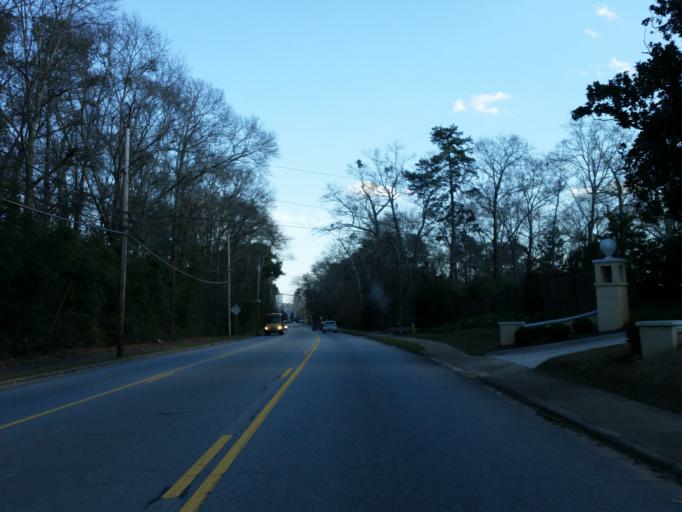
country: US
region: Georgia
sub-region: Monroe County
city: Forsyth
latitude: 33.0291
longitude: -83.9270
